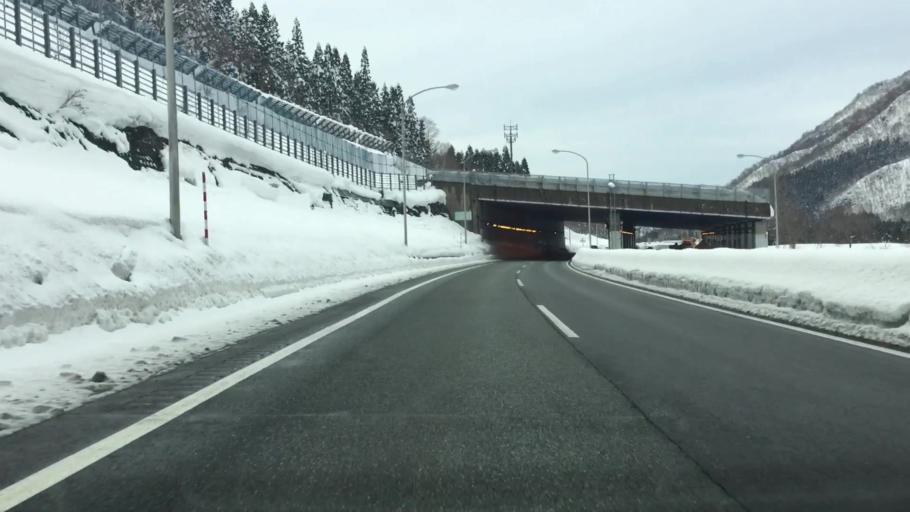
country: JP
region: Niigata
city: Shiozawa
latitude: 36.8694
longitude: 138.8662
